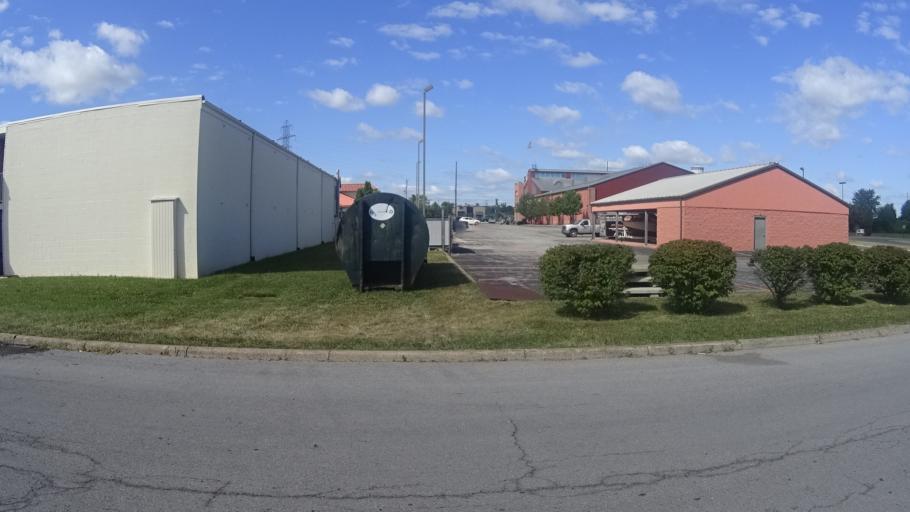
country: US
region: Ohio
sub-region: Erie County
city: Sandusky
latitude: 41.4050
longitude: -82.6580
